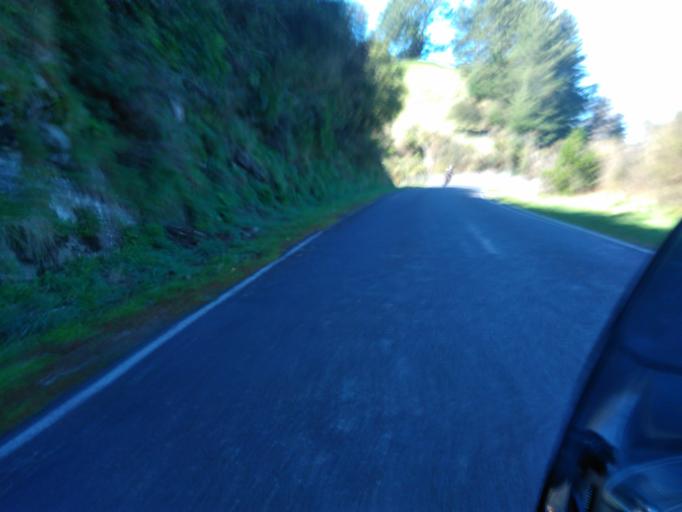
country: NZ
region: Bay of Plenty
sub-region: Opotiki District
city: Opotiki
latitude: -38.3322
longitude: 177.5329
